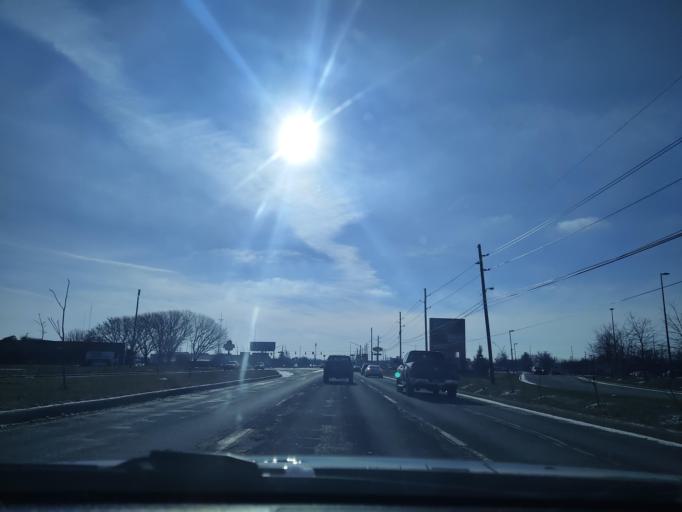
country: US
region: Indiana
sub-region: Boone County
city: Zionsville
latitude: 39.9172
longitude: -86.2254
